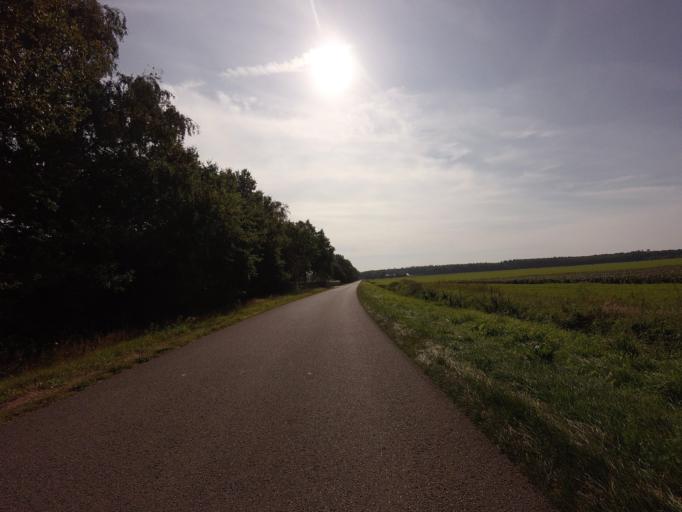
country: NL
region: Drenthe
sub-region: Gemeente Borger-Odoorn
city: Borger
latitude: 52.9322
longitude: 6.7014
